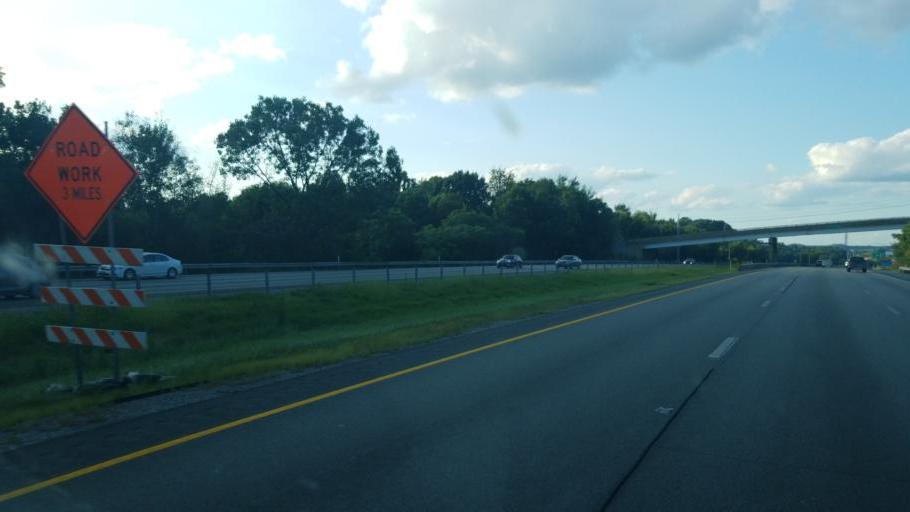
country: US
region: Pennsylvania
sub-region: Allegheny County
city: Bradford Woods
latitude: 40.6398
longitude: -80.0976
